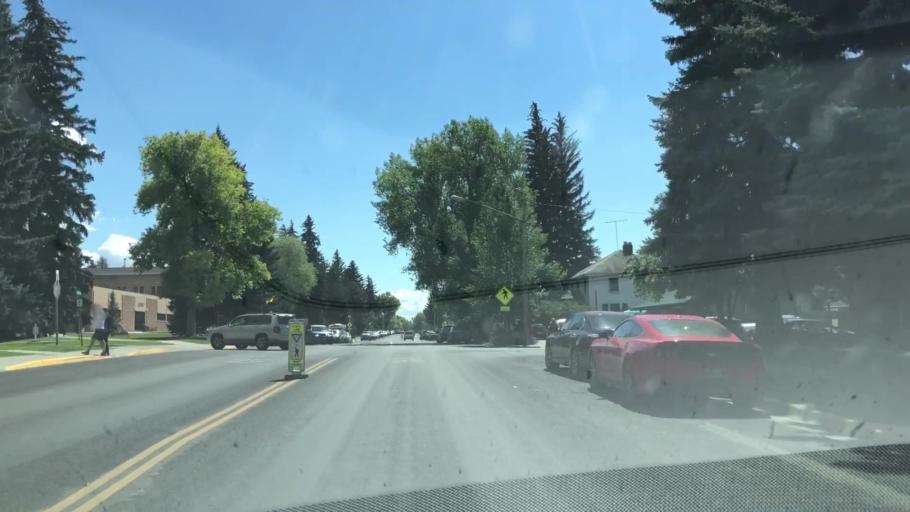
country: US
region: Wyoming
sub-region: Albany County
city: Laramie
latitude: 41.3147
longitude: -105.5853
